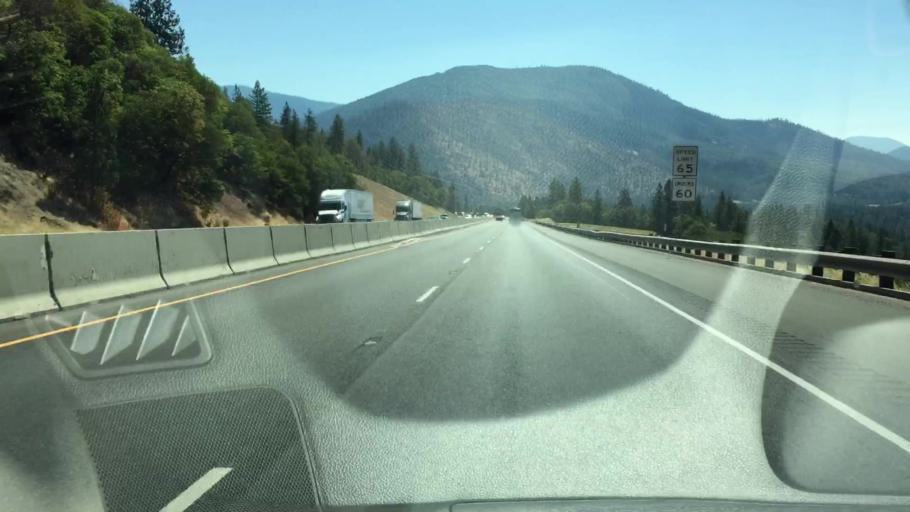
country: US
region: Oregon
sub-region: Josephine County
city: Merlin
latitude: 42.5871
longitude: -123.3878
